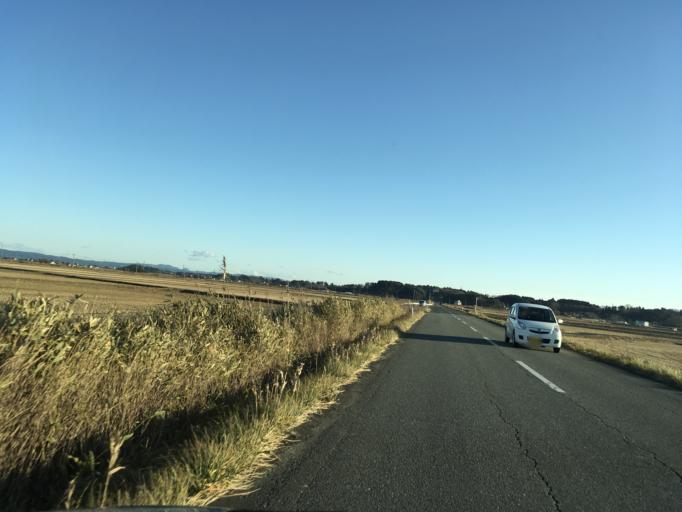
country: JP
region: Miyagi
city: Wakuya
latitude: 38.7296
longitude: 141.1255
